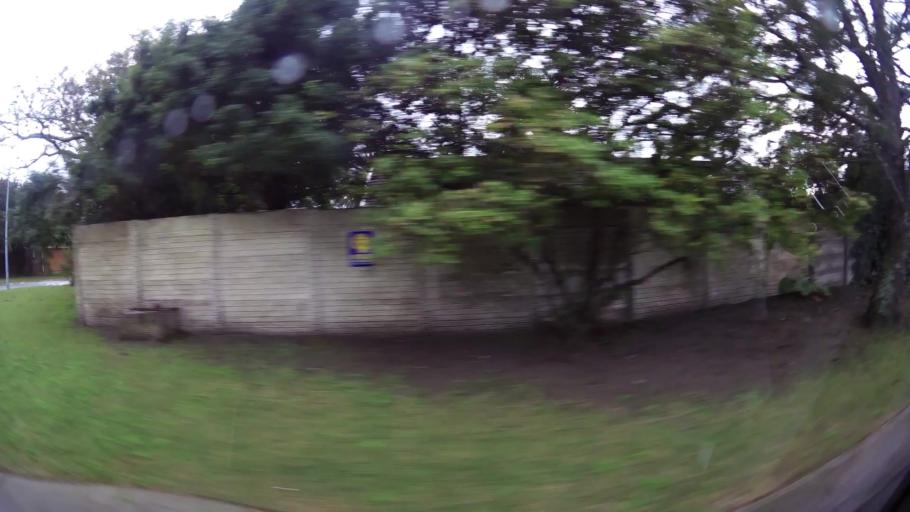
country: ZA
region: Eastern Cape
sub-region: Nelson Mandela Bay Metropolitan Municipality
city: Port Elizabeth
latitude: -33.9934
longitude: 25.5499
